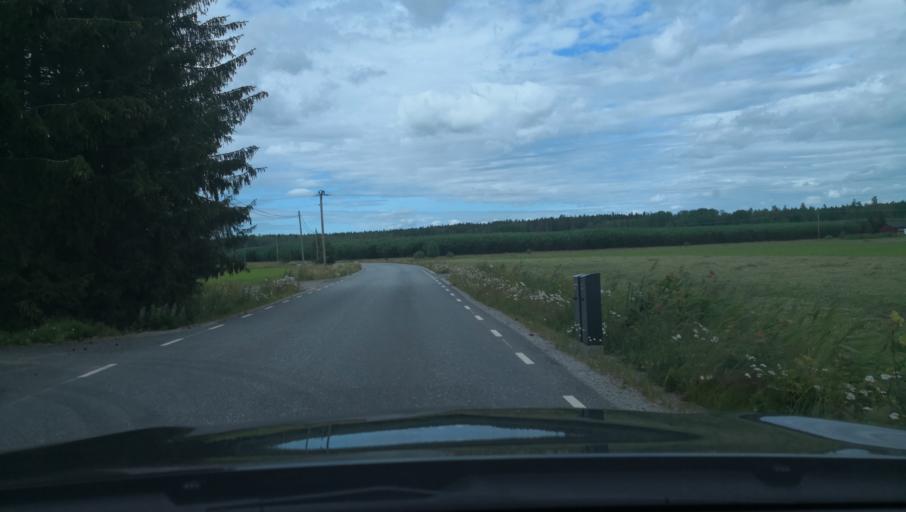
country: SE
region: Vaestmanland
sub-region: Hallstahammars Kommun
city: Hallstahammar
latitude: 59.6053
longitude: 16.1486
